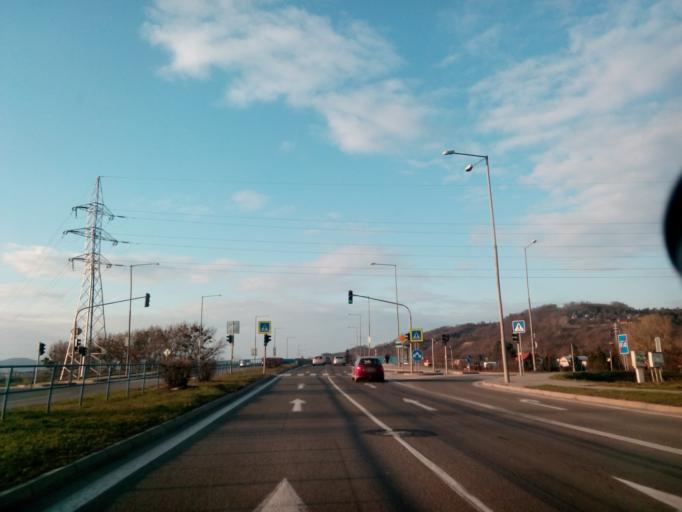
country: SK
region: Kosicky
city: Kosice
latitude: 48.6979
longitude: 21.2803
